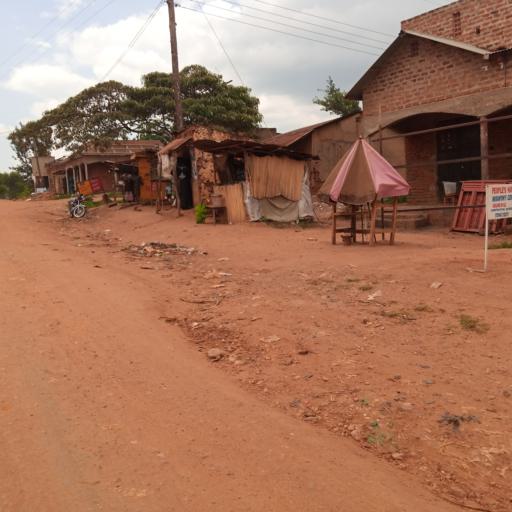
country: UG
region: Eastern Region
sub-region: Mbale District
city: Mbale
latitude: 1.1160
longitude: 34.2032
